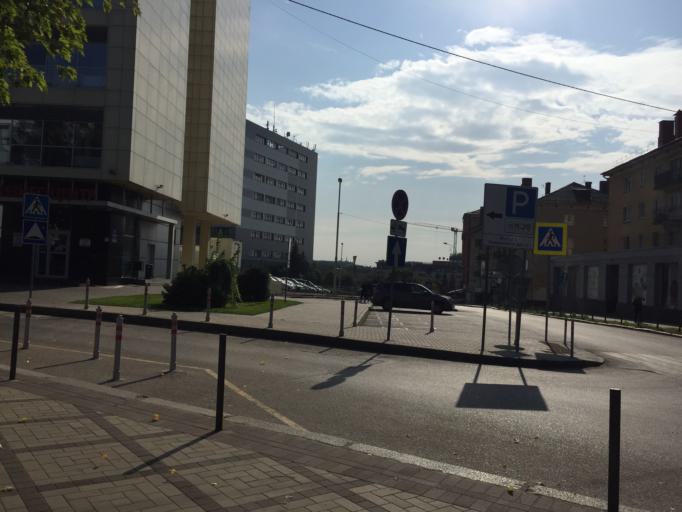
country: RU
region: Kaliningrad
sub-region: Gorod Kaliningrad
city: Kaliningrad
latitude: 54.7119
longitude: 20.5069
